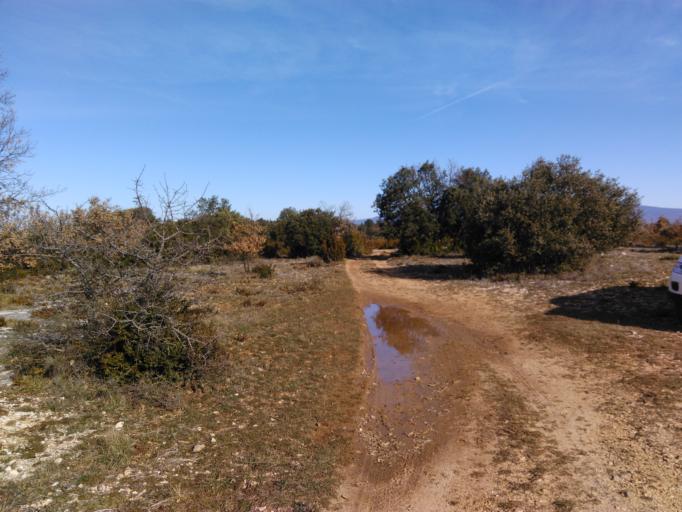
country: FR
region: Provence-Alpes-Cote d'Azur
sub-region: Departement du Vaucluse
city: Venasque
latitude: 43.9600
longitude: 5.1798
